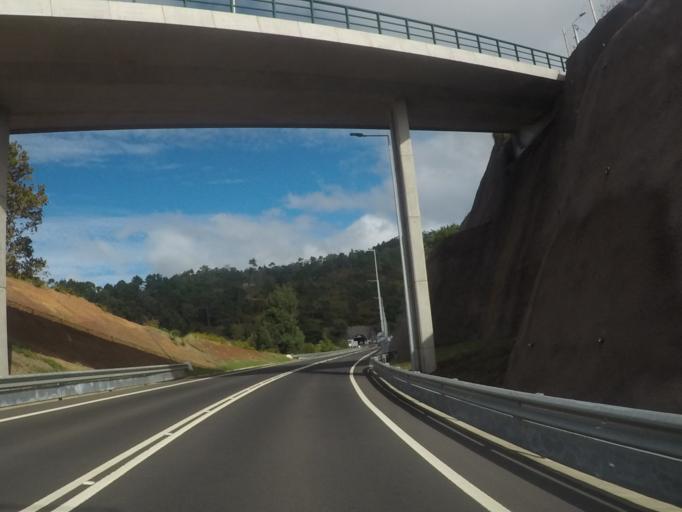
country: PT
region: Madeira
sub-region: Calheta
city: Faja da Ovelha
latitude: 32.7737
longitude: -17.2195
